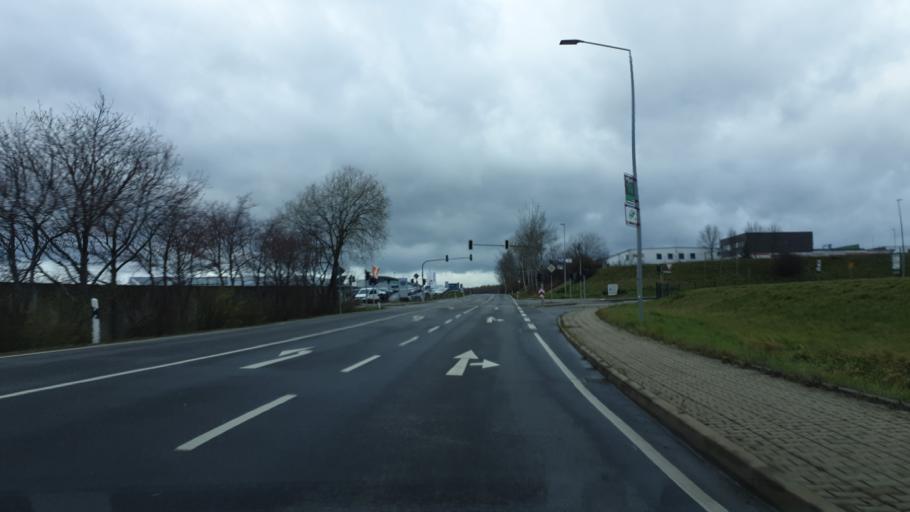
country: DE
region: Saxony
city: Oberlungwitz
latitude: 50.7859
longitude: 12.6861
